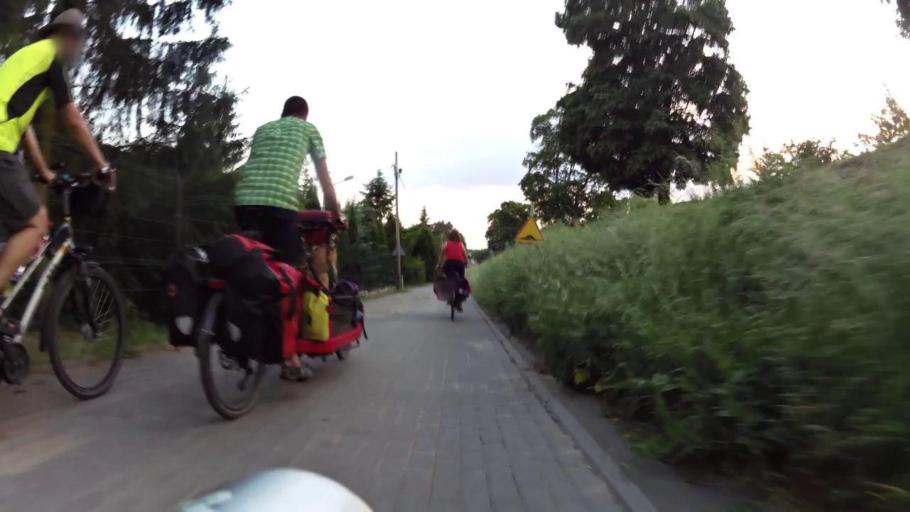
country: PL
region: Kujawsko-Pomorskie
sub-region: Bydgoszcz
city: Fordon
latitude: 53.1510
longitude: 18.2203
